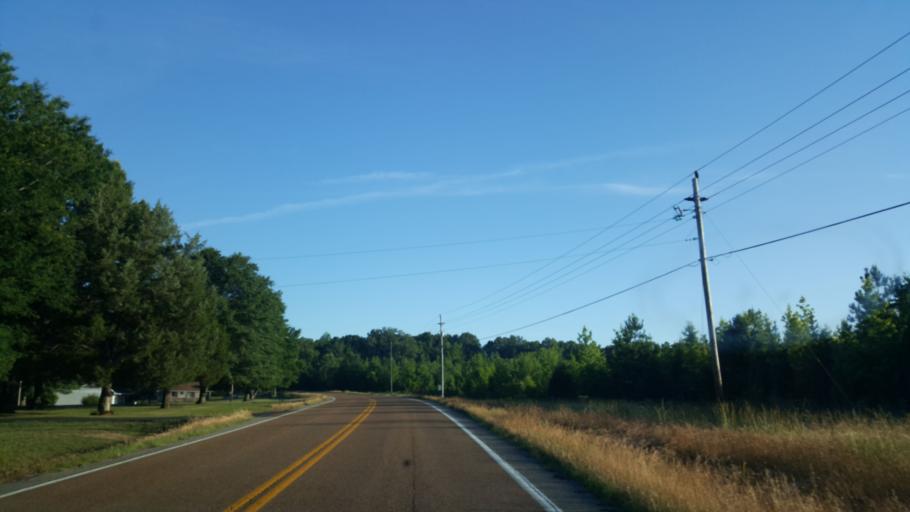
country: US
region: Tennessee
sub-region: McNairy County
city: Adamsville
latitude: 35.3322
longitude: -88.3567
